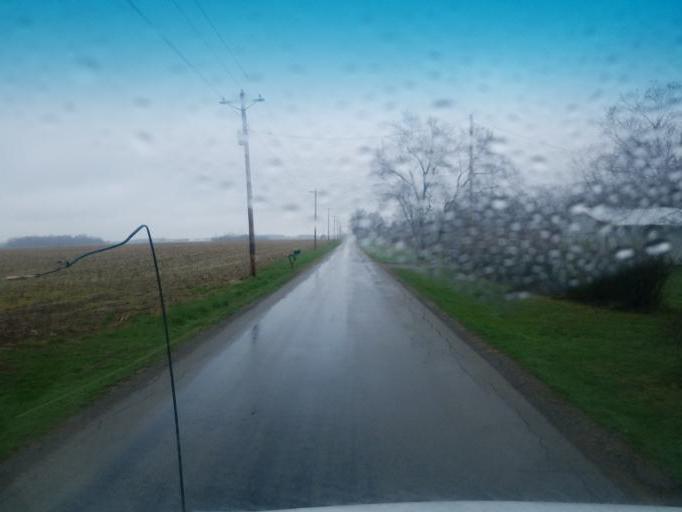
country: US
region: Ohio
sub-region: Seneca County
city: Tiffin
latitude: 40.9644
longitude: -83.1367
